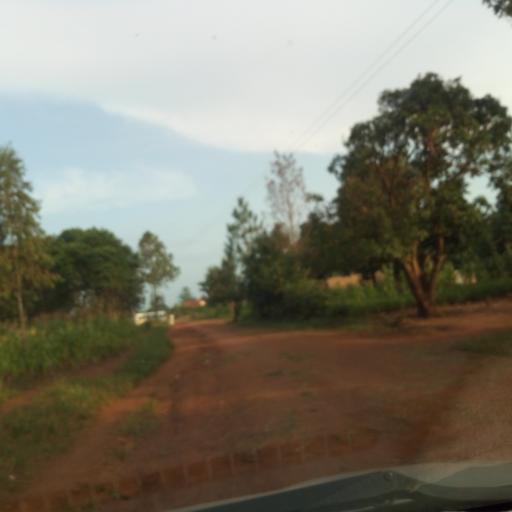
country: UG
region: Western Region
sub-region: Kiryandongo District
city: Kiryandongo
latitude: 1.8053
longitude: 32.0048
